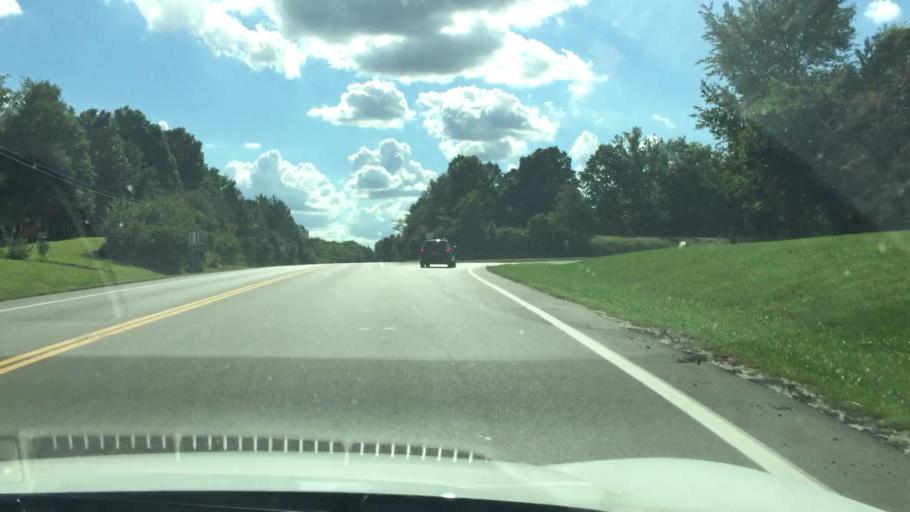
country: US
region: Ohio
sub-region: Clark County
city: Northridge
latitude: 39.9757
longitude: -83.7470
